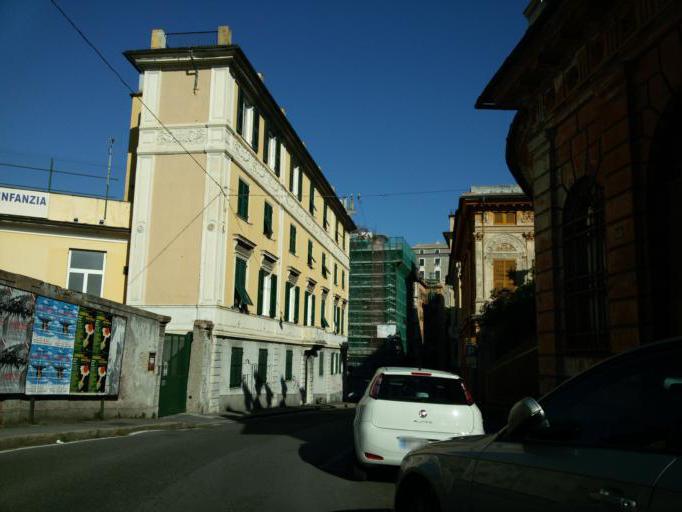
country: IT
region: Liguria
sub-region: Provincia di Genova
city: Genoa
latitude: 44.4103
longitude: 8.9417
